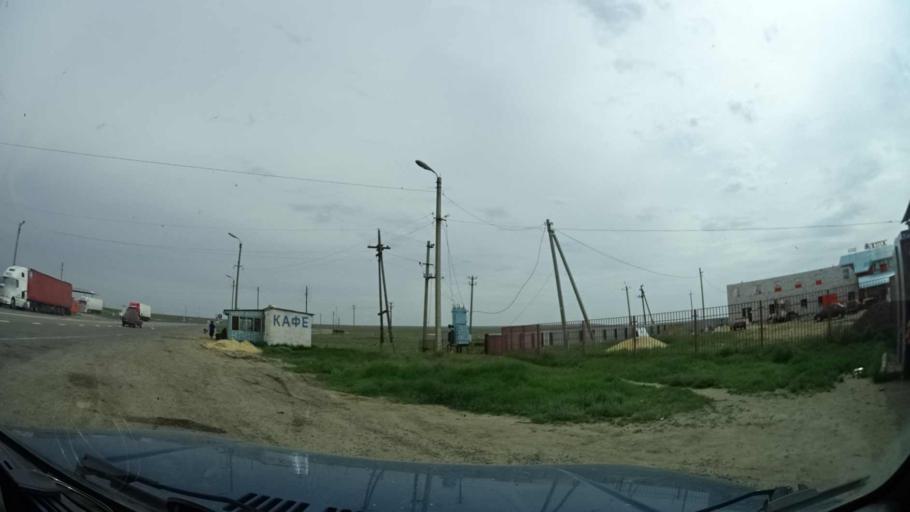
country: RU
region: Kalmykiya
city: Sovetskoye
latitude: 47.2991
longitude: 44.5732
